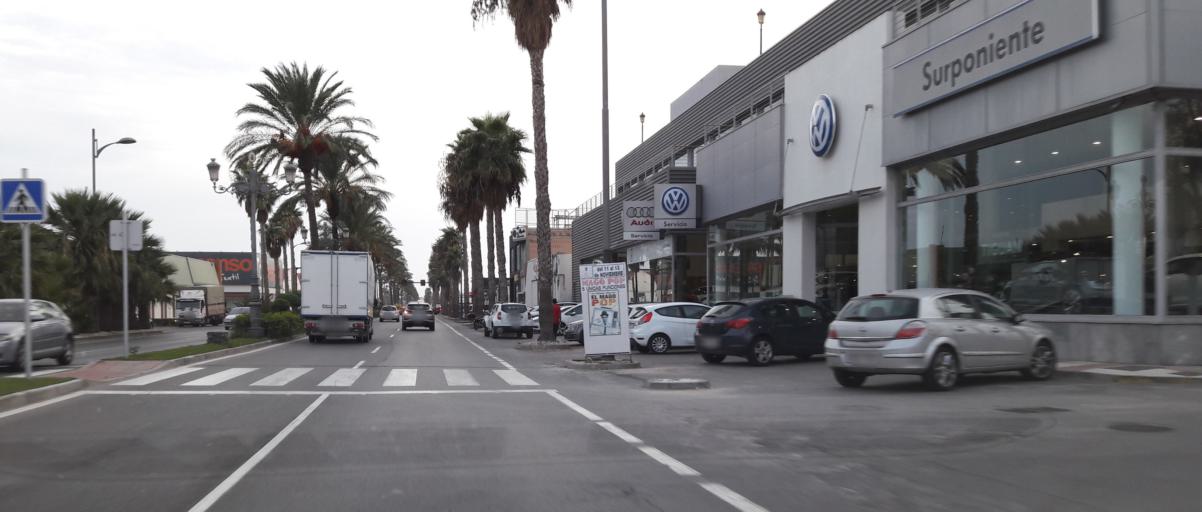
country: ES
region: Andalusia
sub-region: Provincia de Almeria
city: Roquetas de Mar
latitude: 36.7821
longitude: -2.6085
